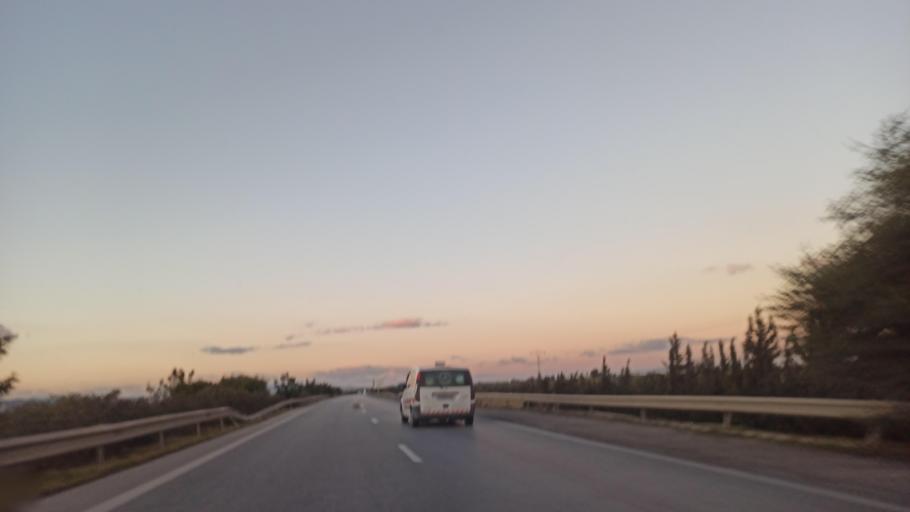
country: TN
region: Nabul
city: Al Hammamat
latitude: 36.2839
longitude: 10.4372
